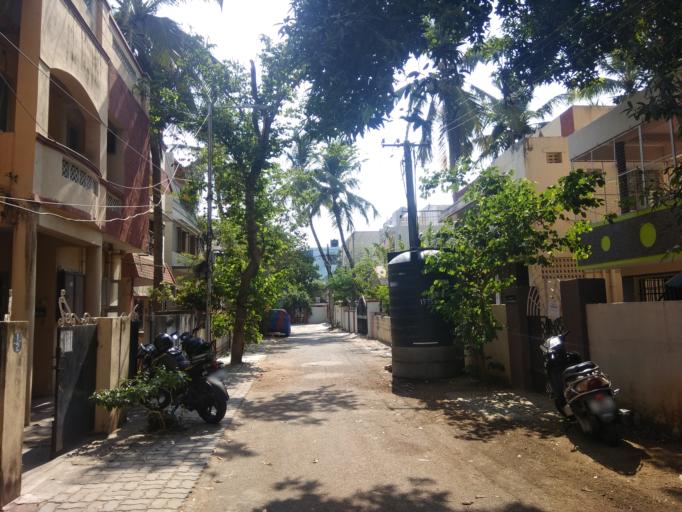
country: IN
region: Tamil Nadu
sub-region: Kancheepuram
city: Perungudi
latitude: 12.9860
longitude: 80.2296
